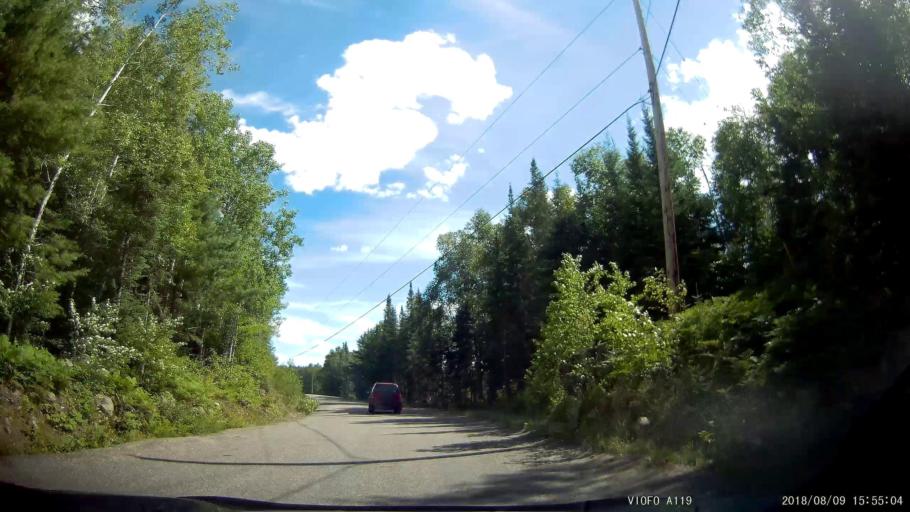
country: CA
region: Ontario
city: Rayside-Balfour
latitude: 46.6048
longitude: -81.5263
